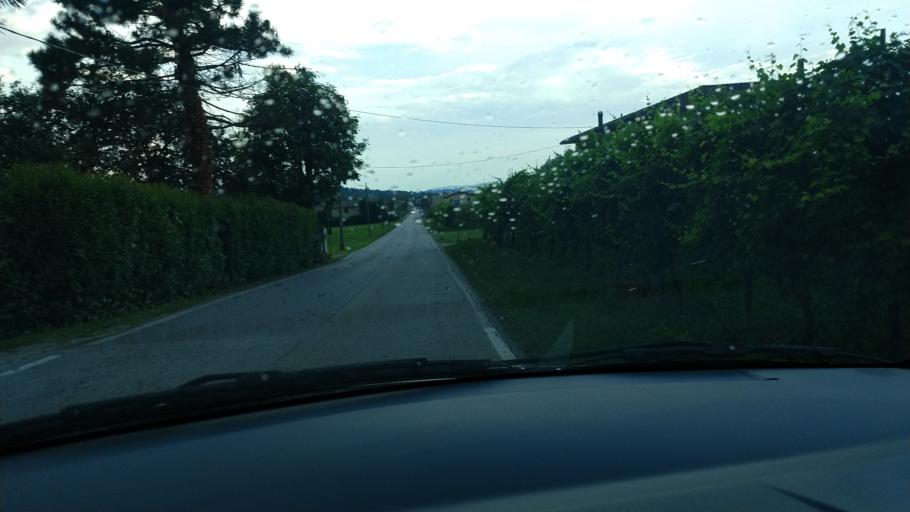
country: IT
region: Veneto
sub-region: Provincia di Vicenza
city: Fara Vicentino
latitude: 45.7435
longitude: 11.5374
